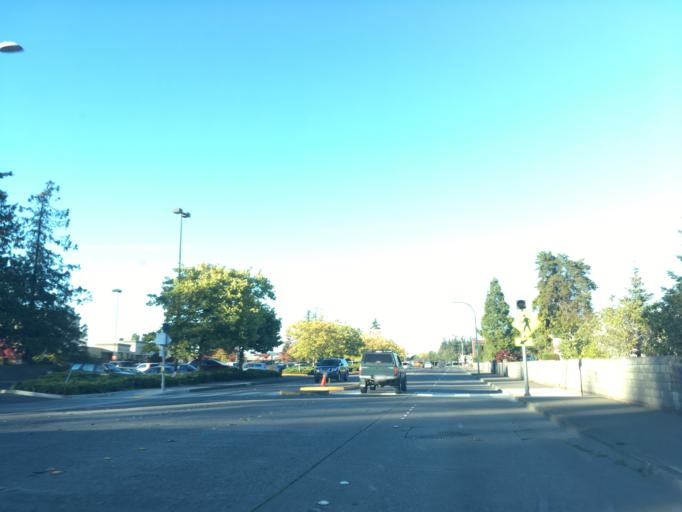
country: US
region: Washington
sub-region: Whatcom County
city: Bellingham
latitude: 48.7419
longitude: -122.4634
